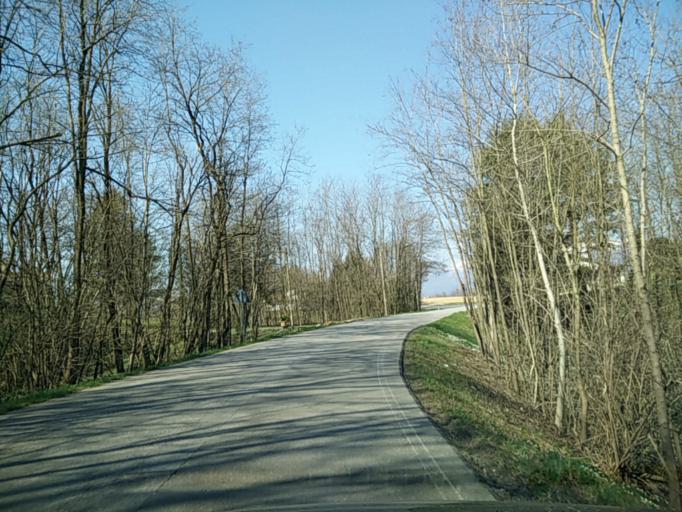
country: IT
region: Veneto
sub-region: Provincia di Treviso
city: Falze di Piave
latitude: 45.8484
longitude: 12.1736
